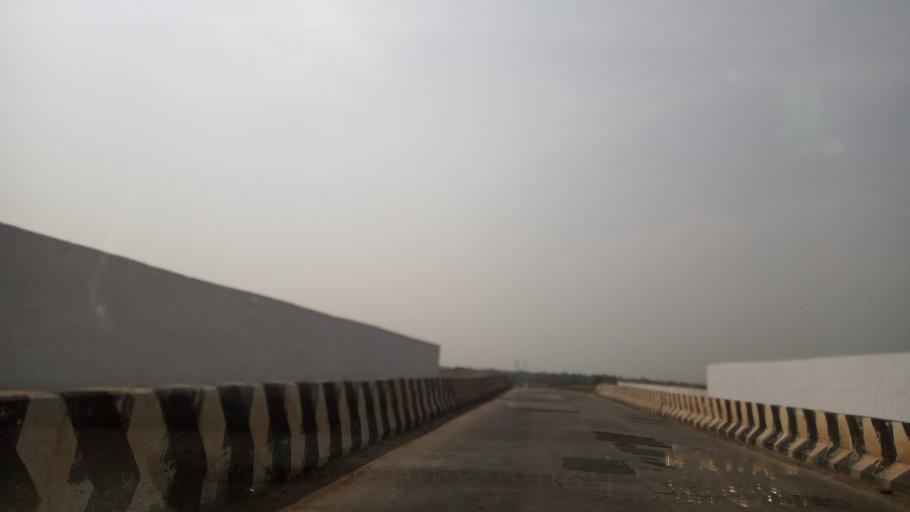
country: IN
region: Tamil Nadu
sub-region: Cuddalore
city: Vriddhachalam
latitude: 11.5145
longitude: 79.3085
